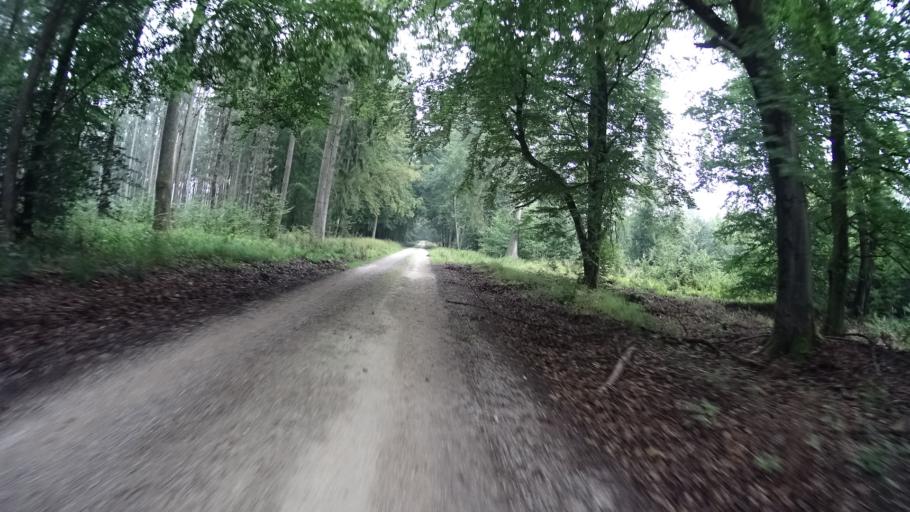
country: DE
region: Bavaria
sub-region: Upper Bavaria
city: Stammham
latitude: 48.8805
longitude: 11.5106
